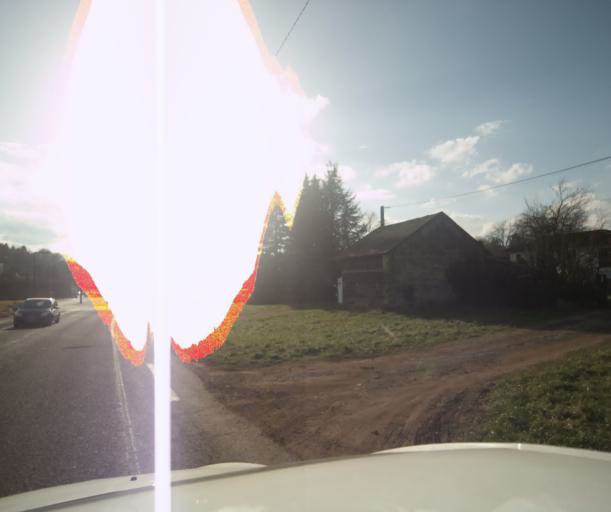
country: FR
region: Franche-Comte
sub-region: Departement du Doubs
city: Besancon
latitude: 47.2517
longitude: 6.0442
